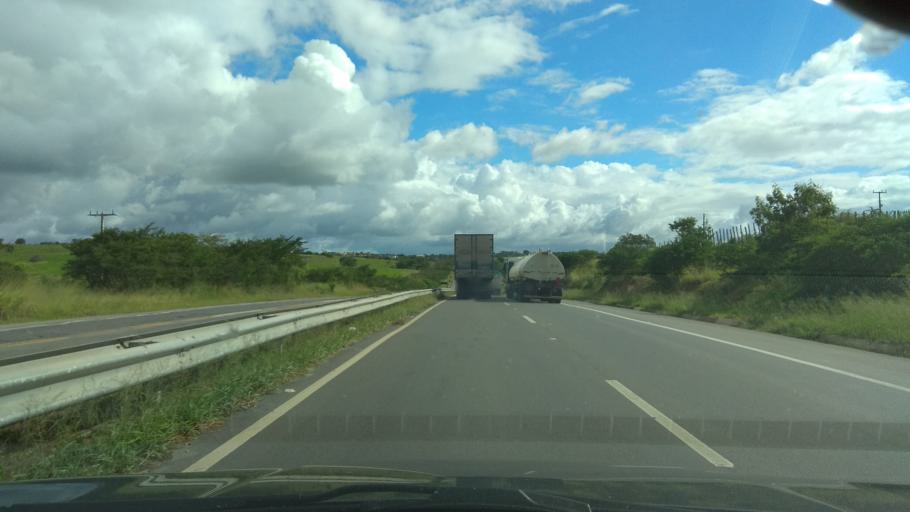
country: BR
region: Bahia
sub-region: Santo Estevao
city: Santo Estevao
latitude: -12.3813
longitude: -39.1284
